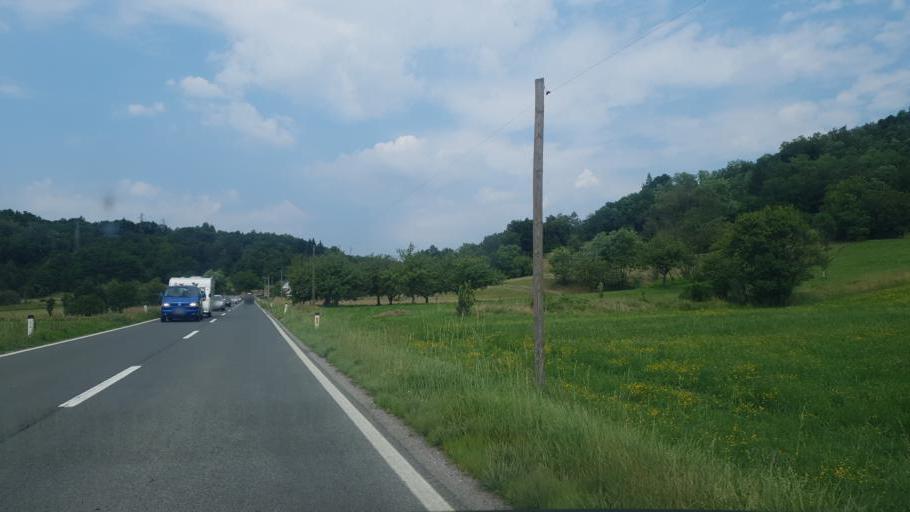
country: SI
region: Ilirska Bistrica
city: Ilirska Bistrica
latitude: 45.5076
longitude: 14.2624
